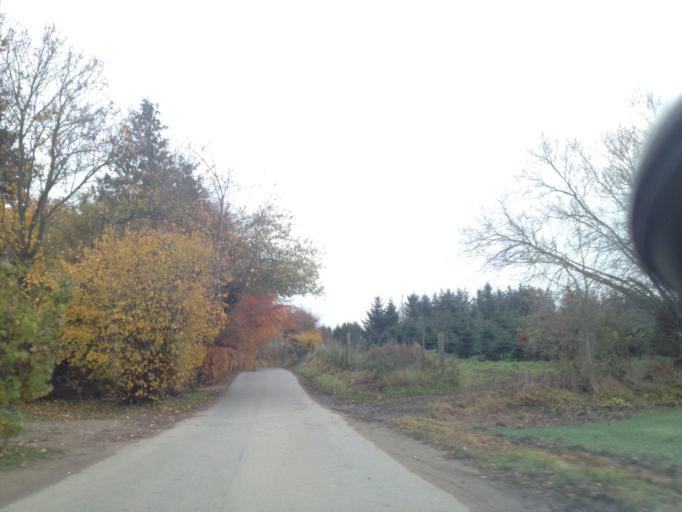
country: DK
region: South Denmark
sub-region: Assens Kommune
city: Vissenbjerg
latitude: 55.4279
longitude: 10.1836
